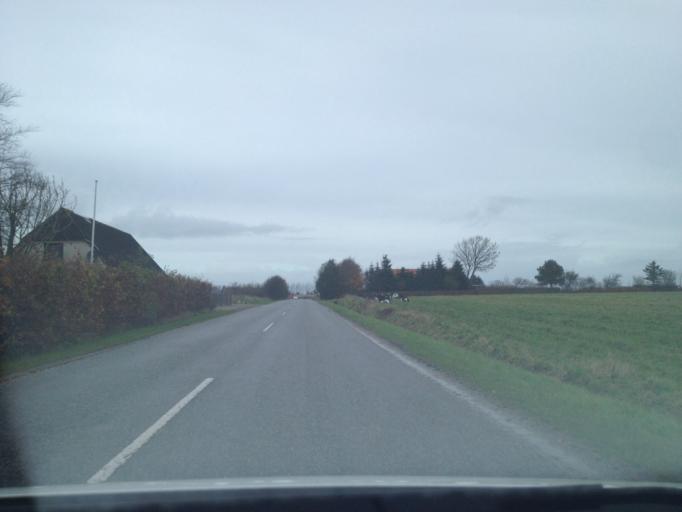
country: DK
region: South Denmark
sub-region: Tonder Kommune
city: Sherrebek
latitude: 55.2283
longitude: 8.8353
